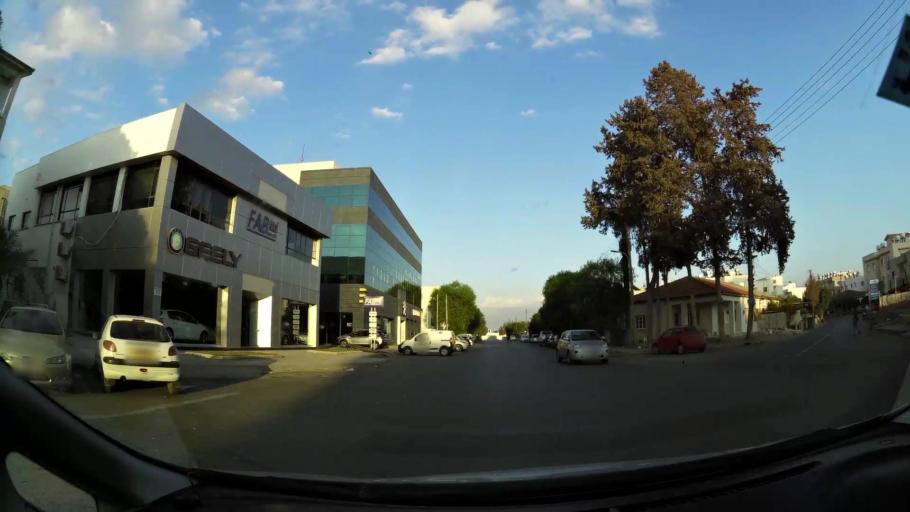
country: CY
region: Lefkosia
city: Nicosia
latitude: 35.1904
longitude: 33.3683
